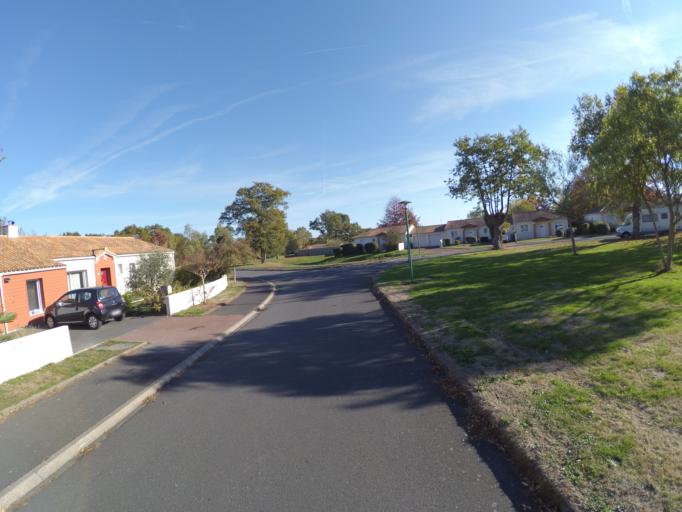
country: FR
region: Pays de la Loire
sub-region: Departement de la Loire-Atlantique
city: Saint-Lumine-de-Clisson
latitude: 47.0876
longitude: -1.3326
